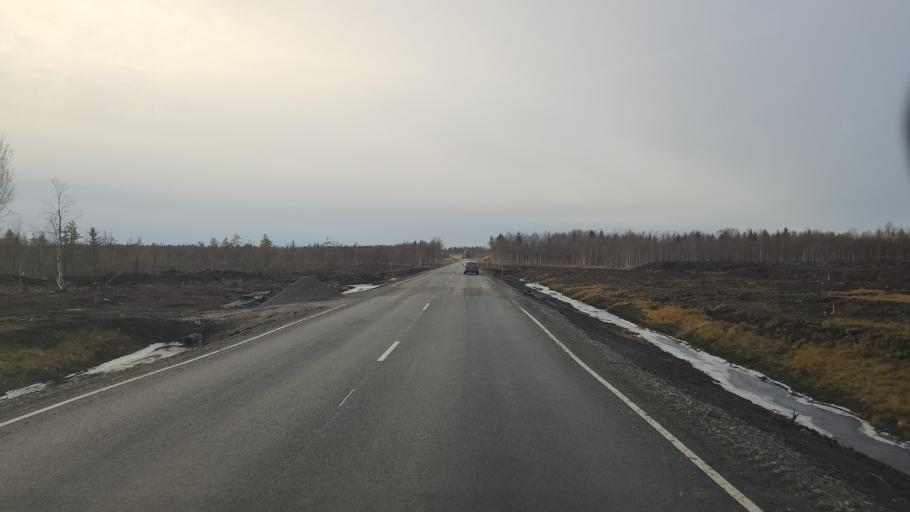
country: FI
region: Lapland
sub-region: Tunturi-Lappi
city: Kittilae
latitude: 67.8646
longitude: 24.9636
